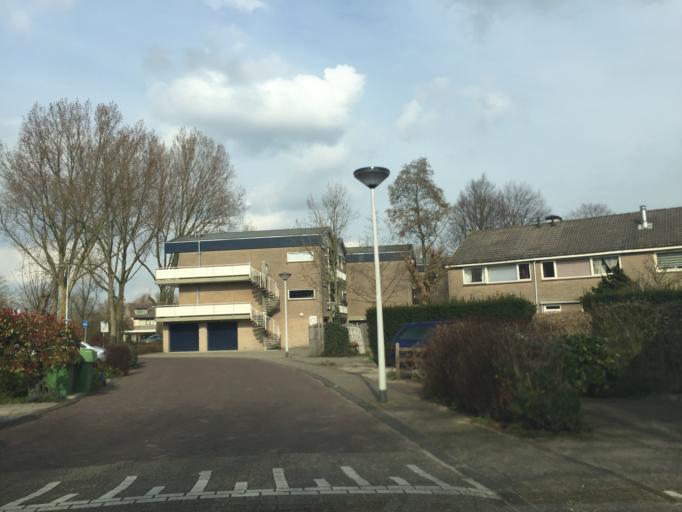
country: NL
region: South Holland
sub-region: Gemeente Leiden
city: Leiden
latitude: 52.1810
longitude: 4.5094
